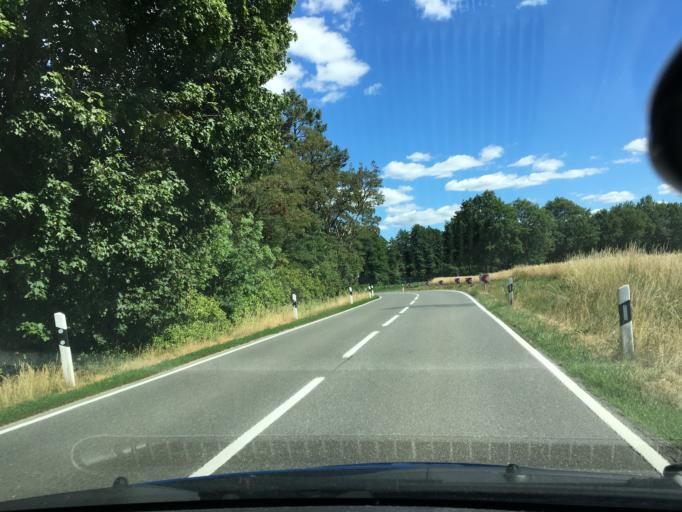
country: DE
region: Lower Saxony
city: Neu Darchau
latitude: 53.1918
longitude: 10.8839
